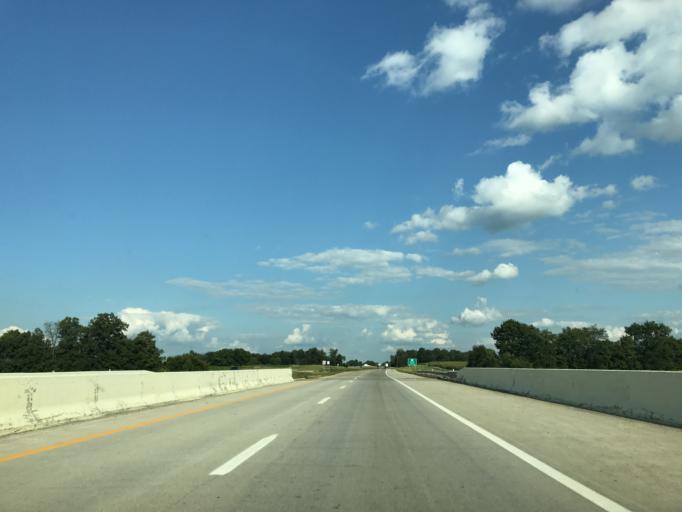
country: US
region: Ohio
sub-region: Wyandot County
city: Upper Sandusky
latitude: 40.8075
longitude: -83.1479
